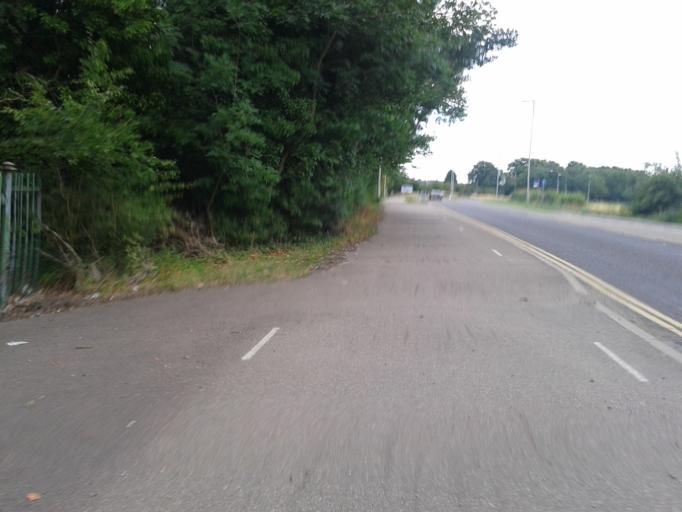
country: GB
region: England
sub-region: Cambridgeshire
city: Sawston
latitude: 52.1670
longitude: 0.1583
